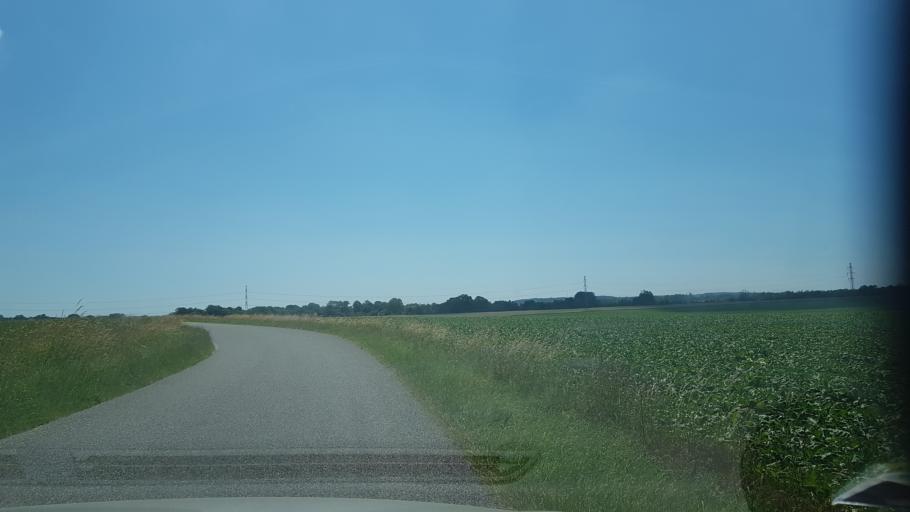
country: DK
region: Zealand
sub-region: Kalundborg Kommune
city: Svebolle
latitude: 55.6943
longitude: 11.2995
